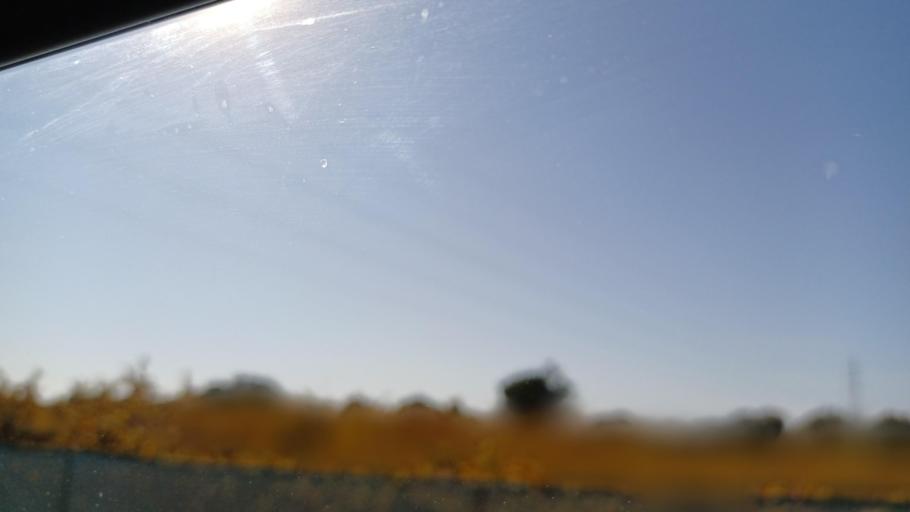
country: CY
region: Larnaka
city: Kolossi
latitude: 34.6618
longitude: 32.9358
